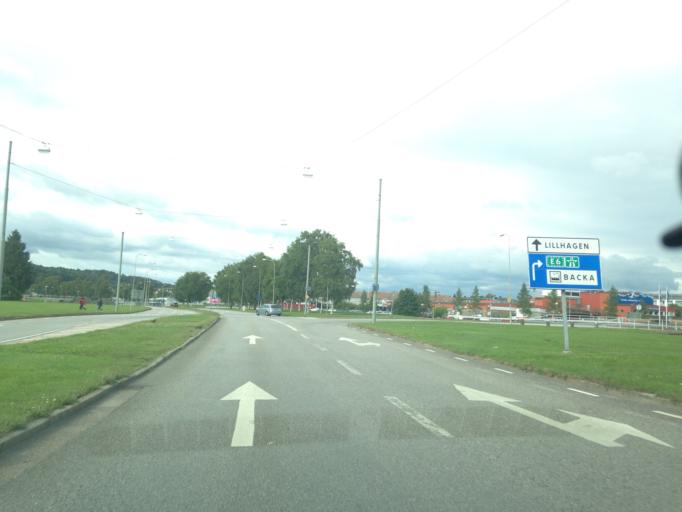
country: SE
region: Vaestra Goetaland
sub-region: Goteborg
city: Goeteborg
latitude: 57.7482
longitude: 11.9799
